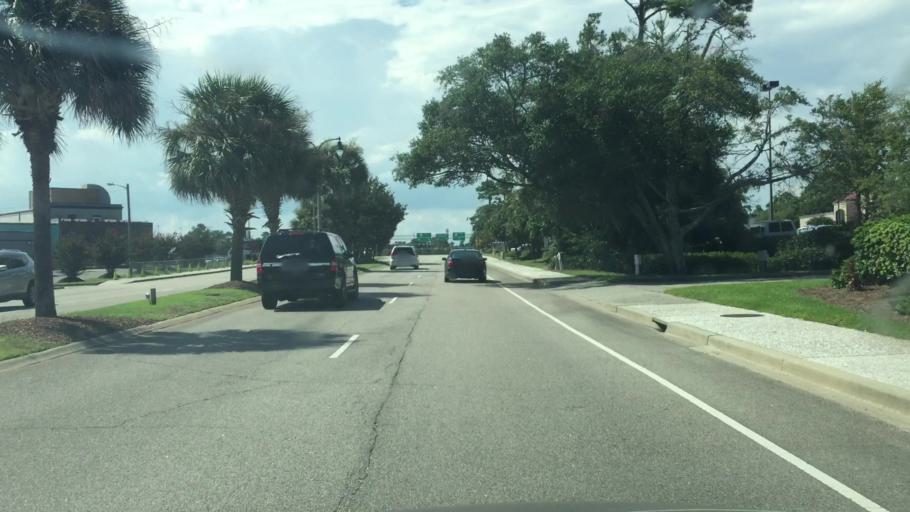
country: US
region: South Carolina
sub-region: Horry County
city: North Myrtle Beach
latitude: 33.8257
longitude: -78.6768
